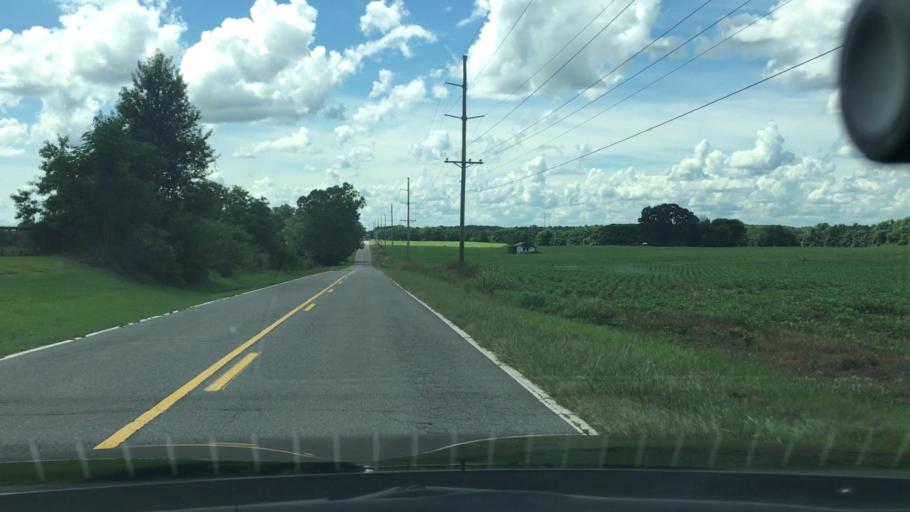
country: US
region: Georgia
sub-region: Putnam County
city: Jefferson
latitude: 33.3693
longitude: -83.2893
